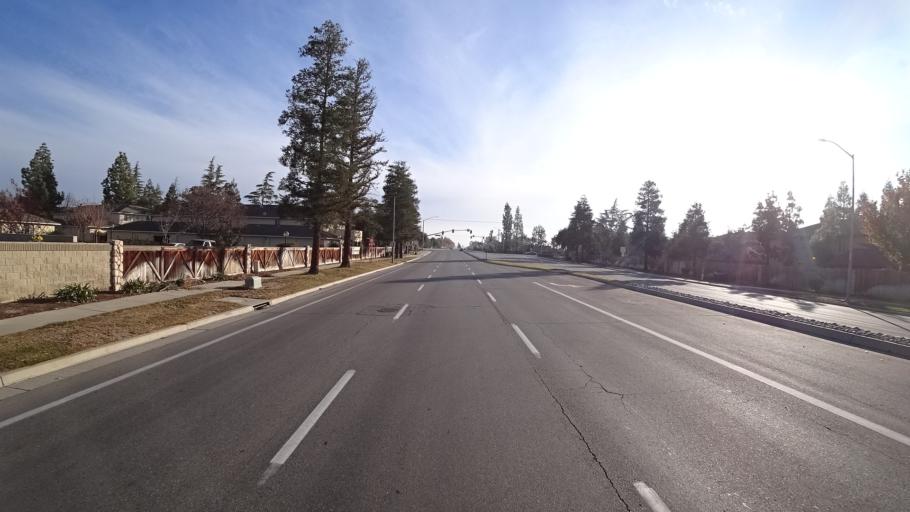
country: US
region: California
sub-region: Kern County
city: Greenacres
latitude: 35.4015
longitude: -119.0760
